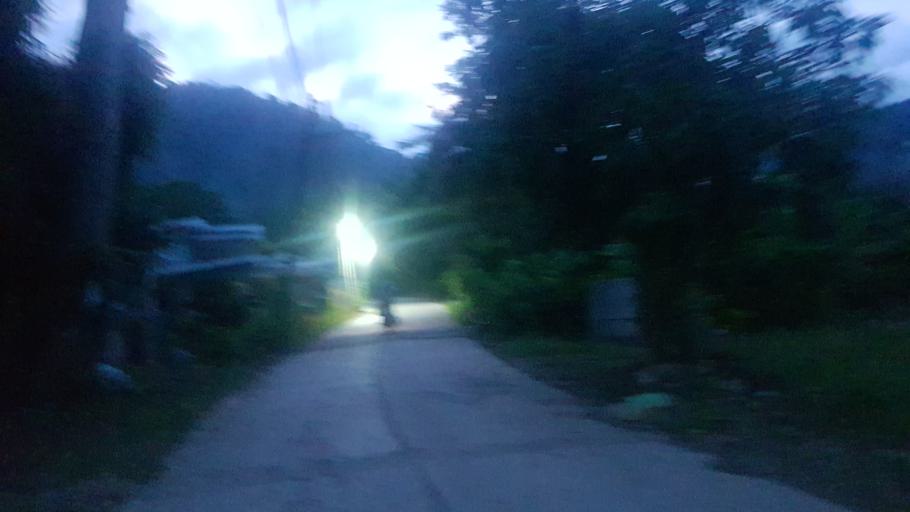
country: TH
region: Phangnga
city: Takua Pa
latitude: 8.9118
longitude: 98.5272
